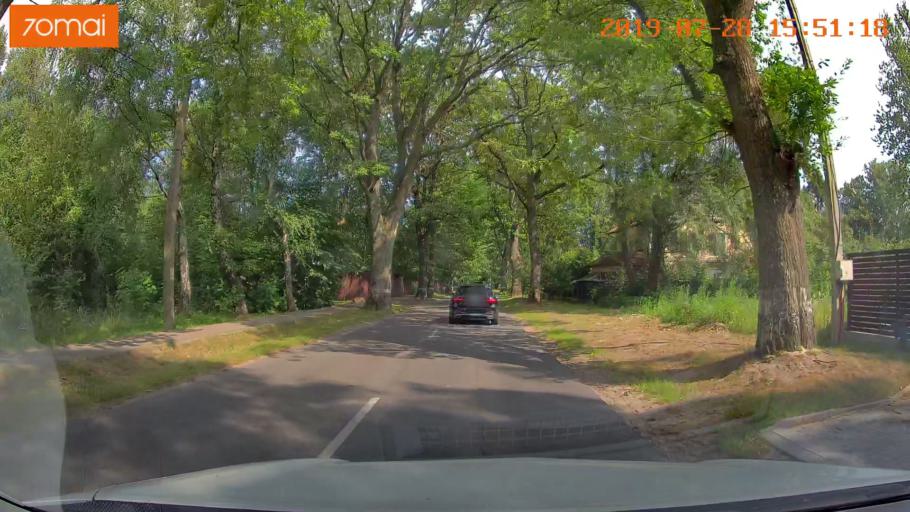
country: RU
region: Kaliningrad
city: Otradnoye
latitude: 54.9414
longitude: 20.1034
